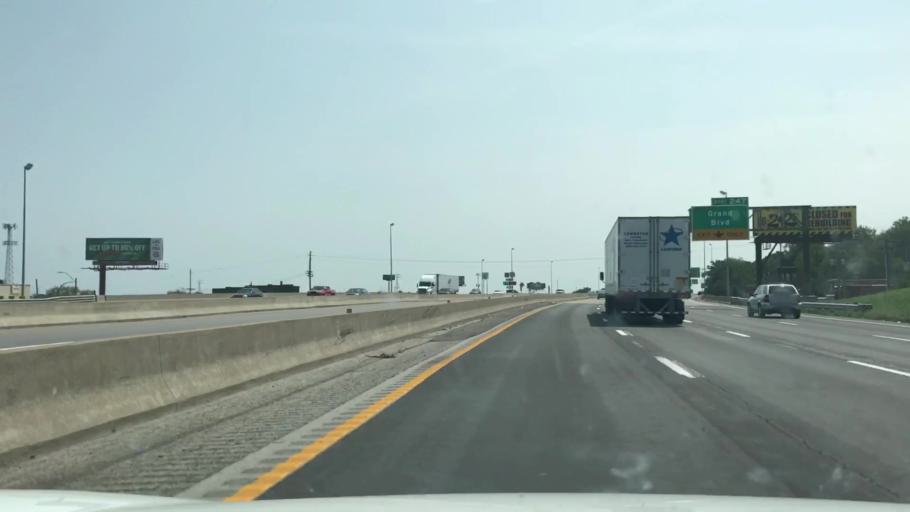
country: US
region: Illinois
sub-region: Madison County
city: Venice
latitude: 38.6765
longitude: -90.2071
